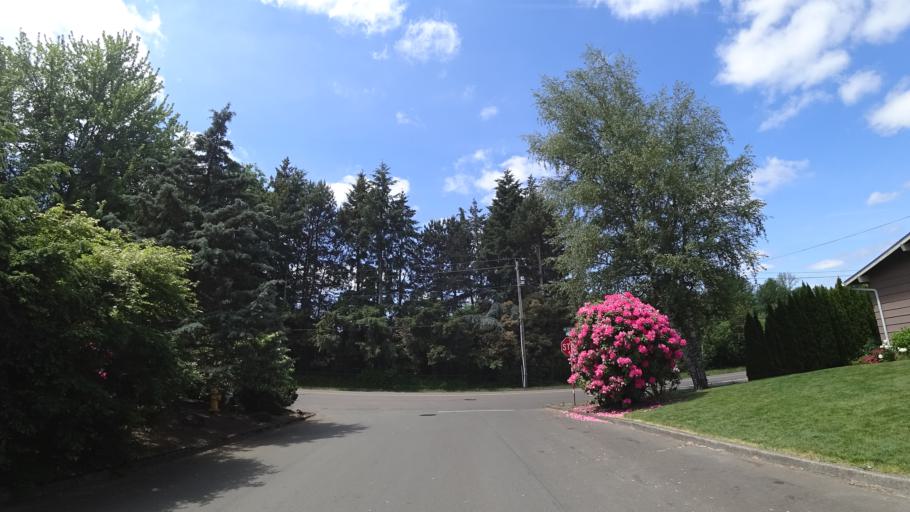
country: US
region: Oregon
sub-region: Washington County
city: Tigard
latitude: 45.4339
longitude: -122.7997
